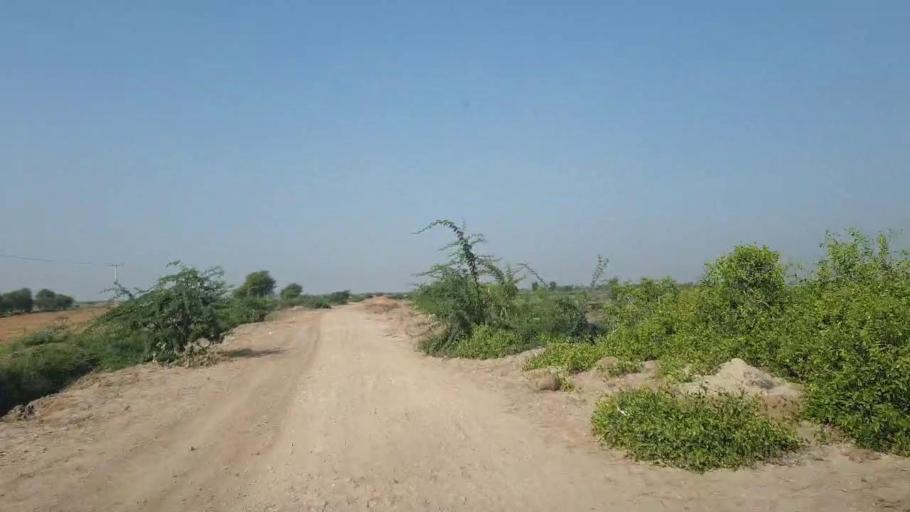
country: PK
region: Sindh
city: Badin
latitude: 24.5193
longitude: 68.7776
